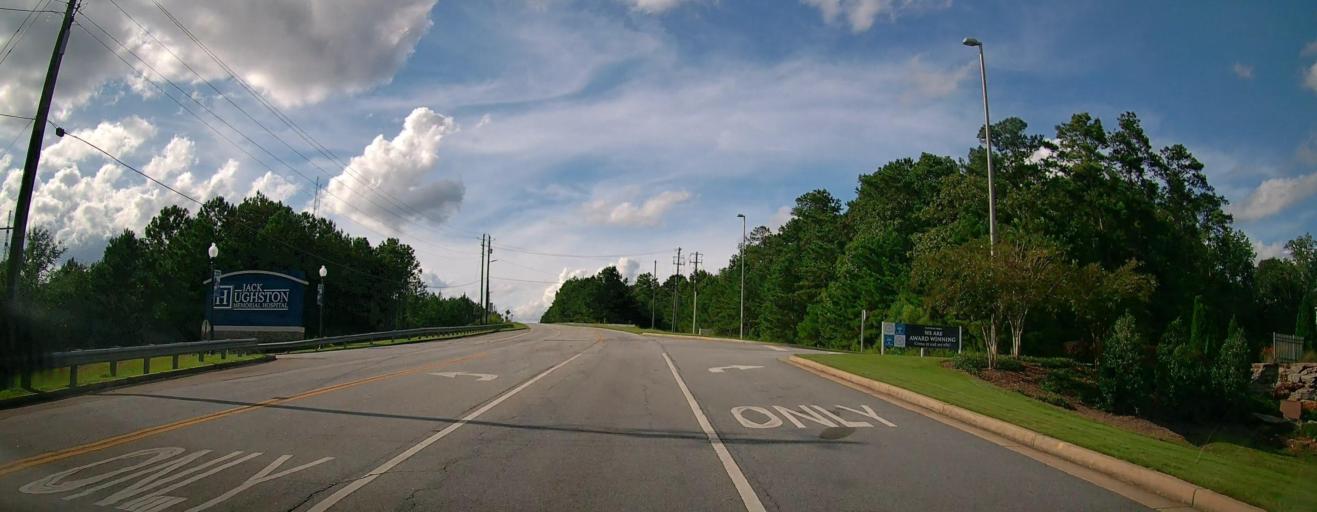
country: US
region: Alabama
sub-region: Russell County
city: Phenix City
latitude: 32.5085
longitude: -85.0053
